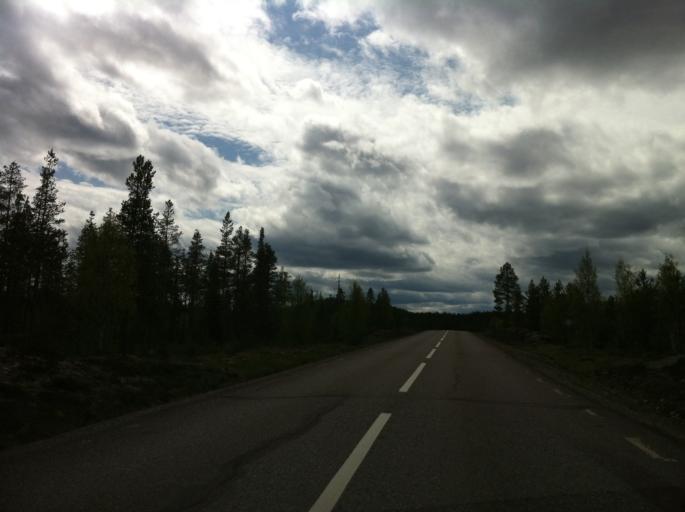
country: NO
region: Hedmark
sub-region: Trysil
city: Innbygda
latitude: 61.5798
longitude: 13.1159
